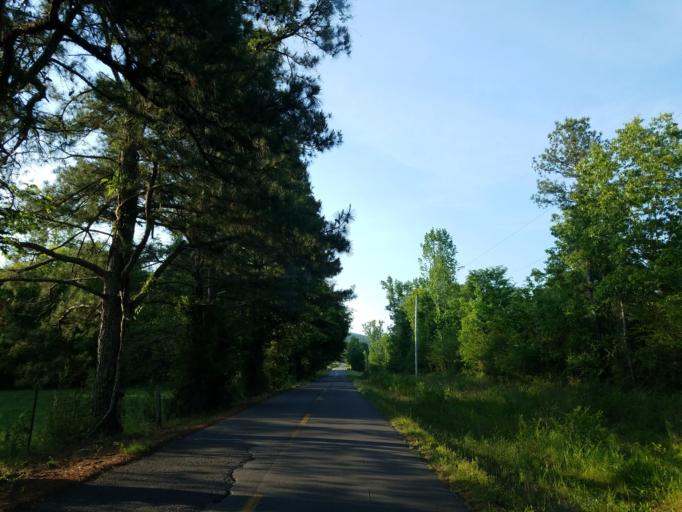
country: US
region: Georgia
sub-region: Gordon County
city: Calhoun
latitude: 34.5418
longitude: -85.1077
